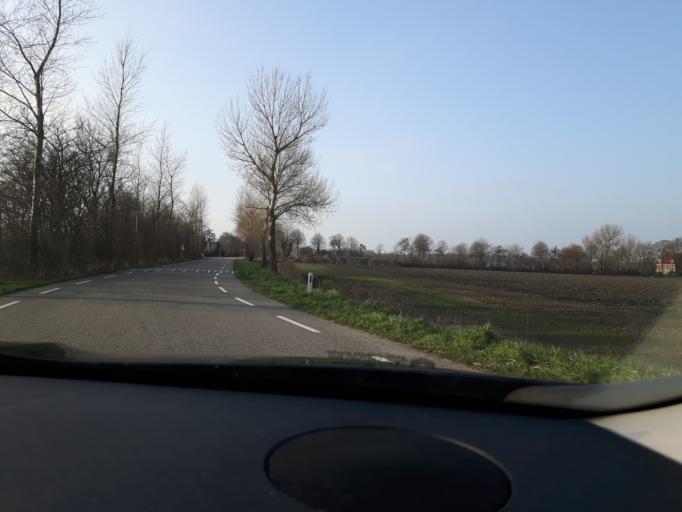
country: NL
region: Zeeland
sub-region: Gemeente Veere
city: Veere
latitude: 51.5792
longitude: 3.6021
